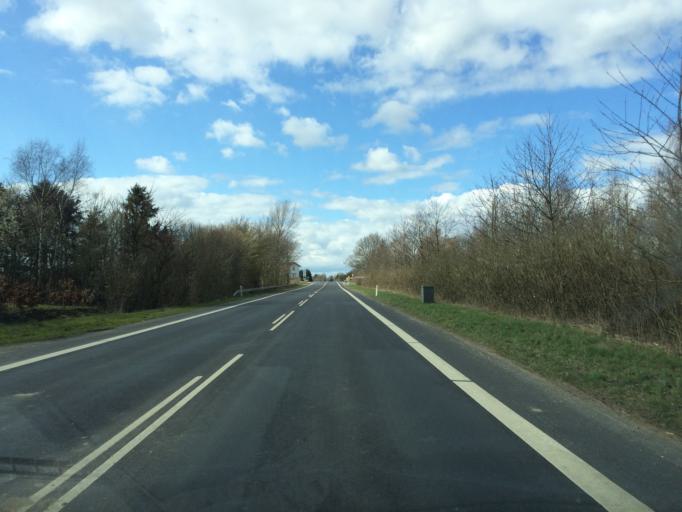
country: DK
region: South Denmark
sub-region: Assens Kommune
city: Arup
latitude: 55.4210
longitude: 10.0366
